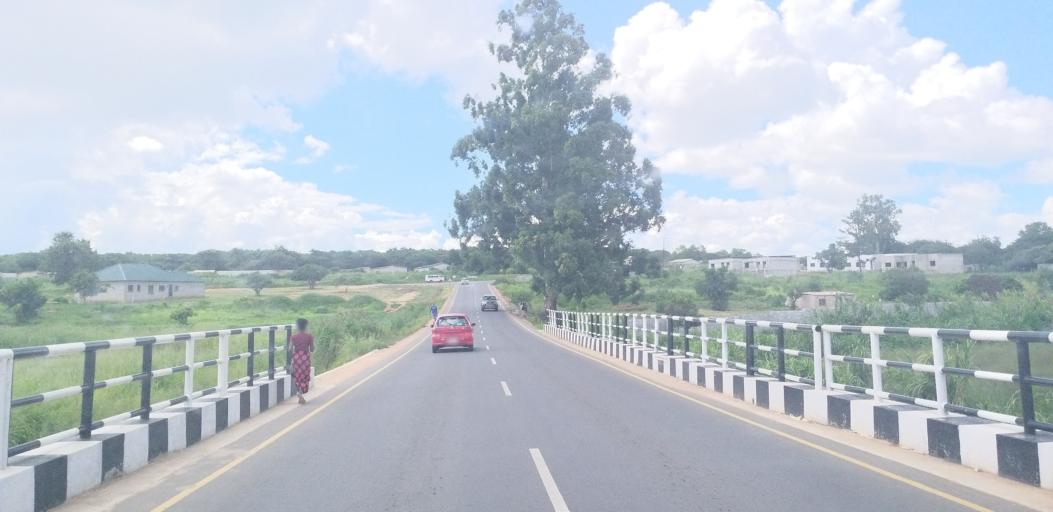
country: ZM
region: Lusaka
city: Lusaka
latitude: -15.3341
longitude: 28.3297
